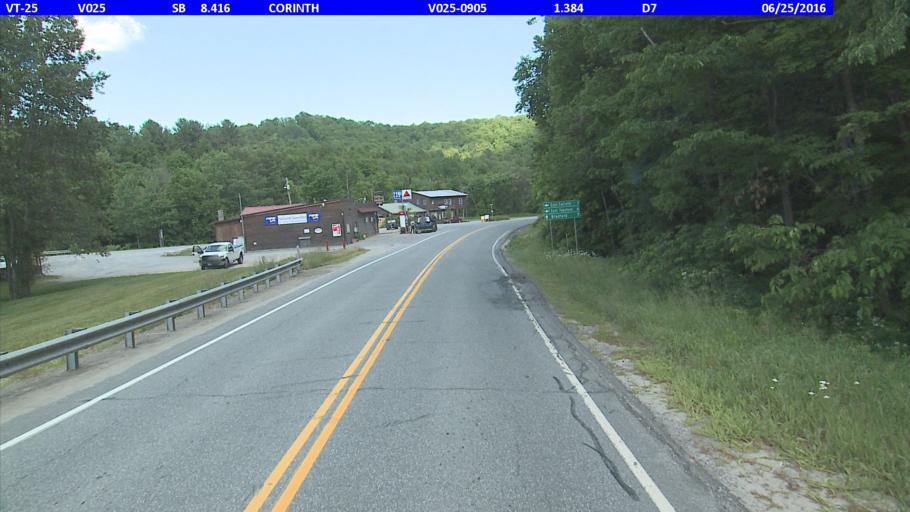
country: US
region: New Hampshire
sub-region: Grafton County
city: Haverhill
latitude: 44.0548
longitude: -72.2221
